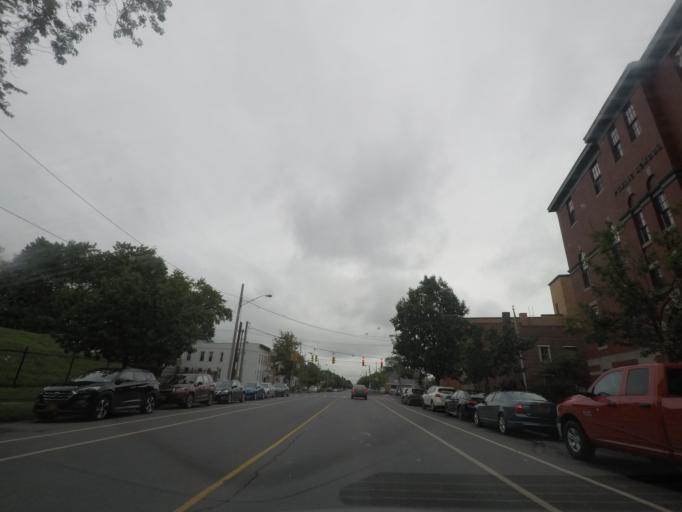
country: US
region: New York
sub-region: Albany County
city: West Albany
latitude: 42.6685
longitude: -73.7747
